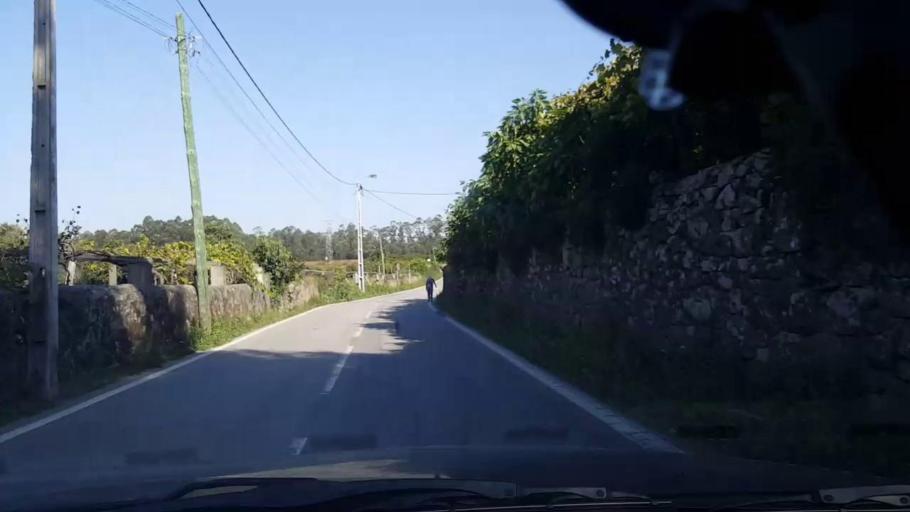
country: PT
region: Porto
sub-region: Vila do Conde
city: Arvore
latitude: 41.3153
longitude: -8.6789
